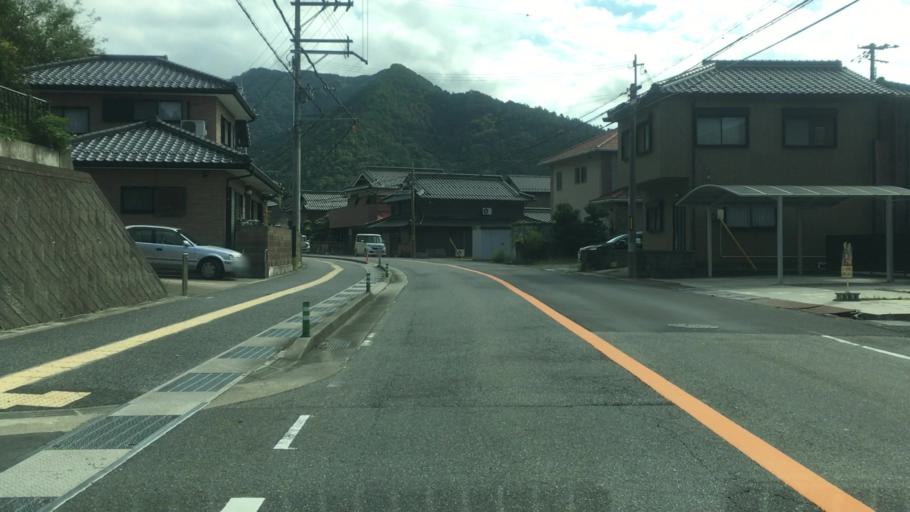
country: JP
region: Kyoto
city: Fukuchiyama
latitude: 35.1498
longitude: 135.0592
